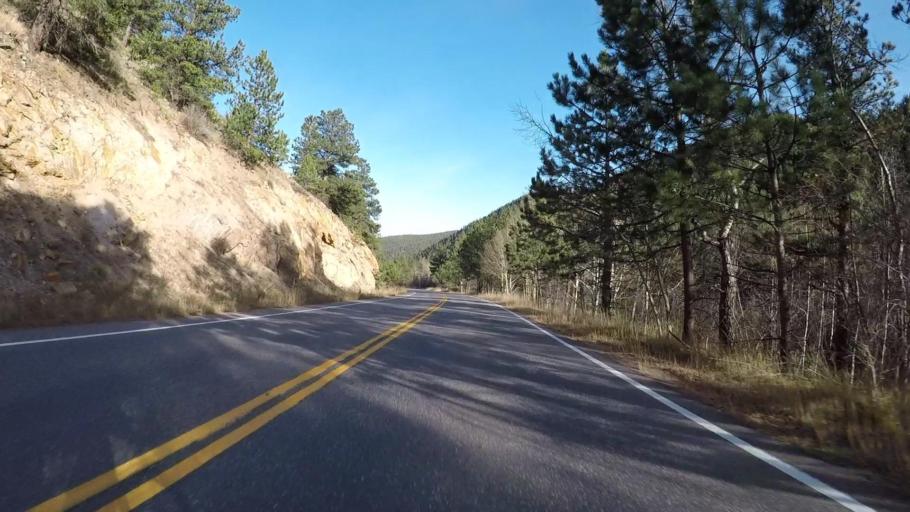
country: US
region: Colorado
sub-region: Boulder County
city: Nederland
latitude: 40.0682
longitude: -105.4432
